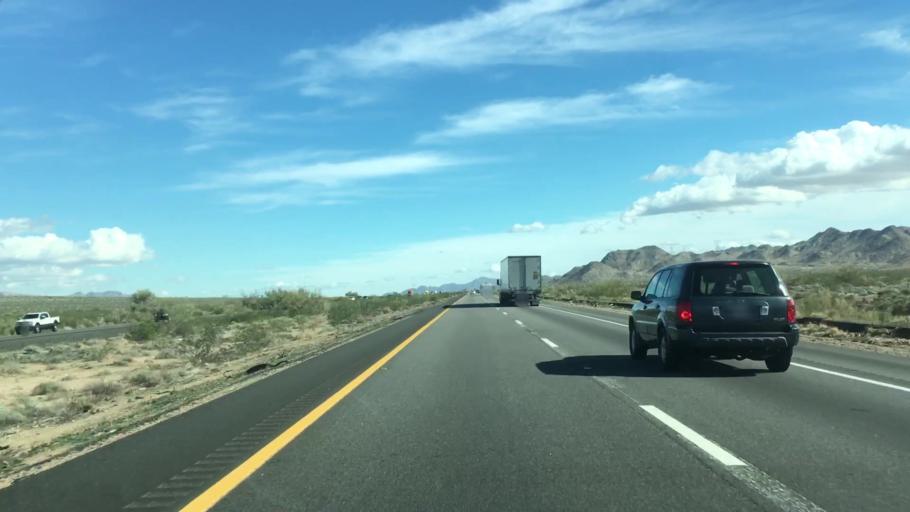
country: US
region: California
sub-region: Riverside County
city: Mecca
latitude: 33.6599
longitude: -115.7545
